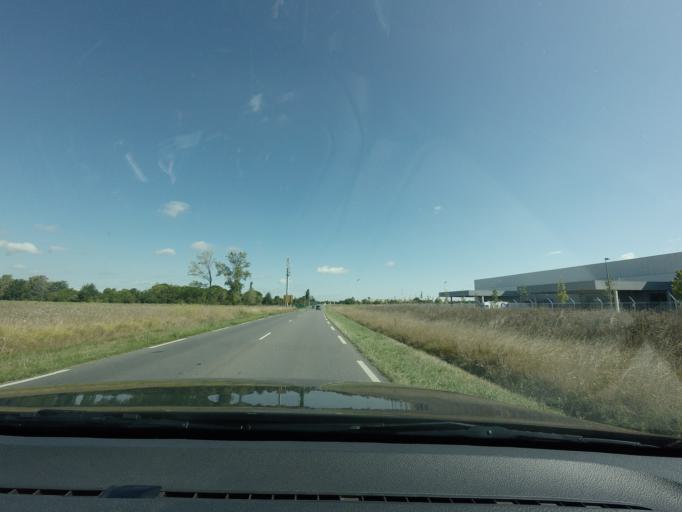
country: FR
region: Midi-Pyrenees
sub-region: Departement de la Haute-Garonne
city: Cornebarrieu
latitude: 43.6318
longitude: 1.3319
